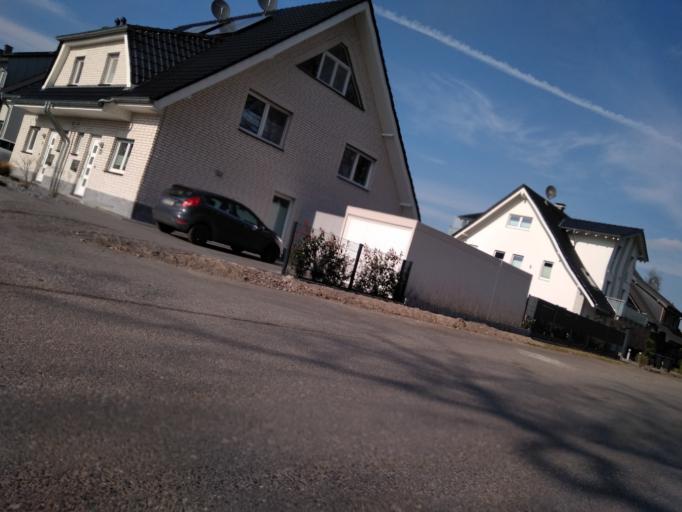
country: DE
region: North Rhine-Westphalia
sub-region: Regierungsbezirk Munster
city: Gladbeck
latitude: 51.5927
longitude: 6.9329
